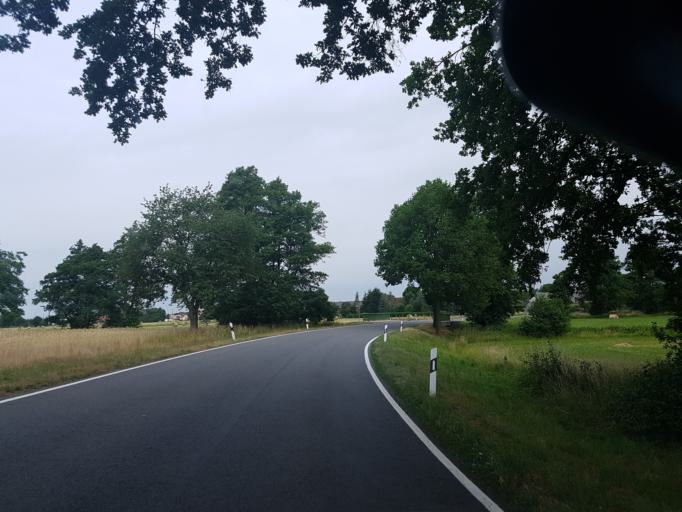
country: DE
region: Brandenburg
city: Schonewalde
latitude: 51.7006
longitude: 13.6057
